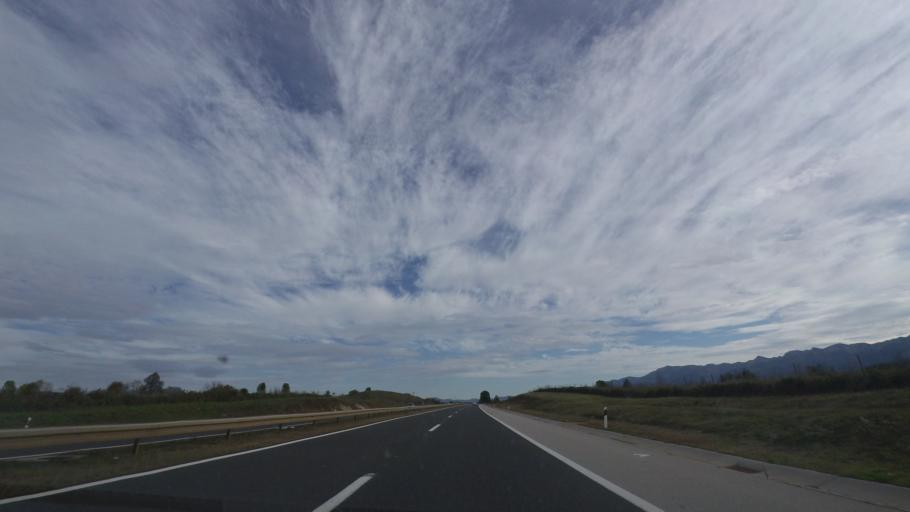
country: HR
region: Licko-Senjska
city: Gospic
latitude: 44.4978
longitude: 15.5348
